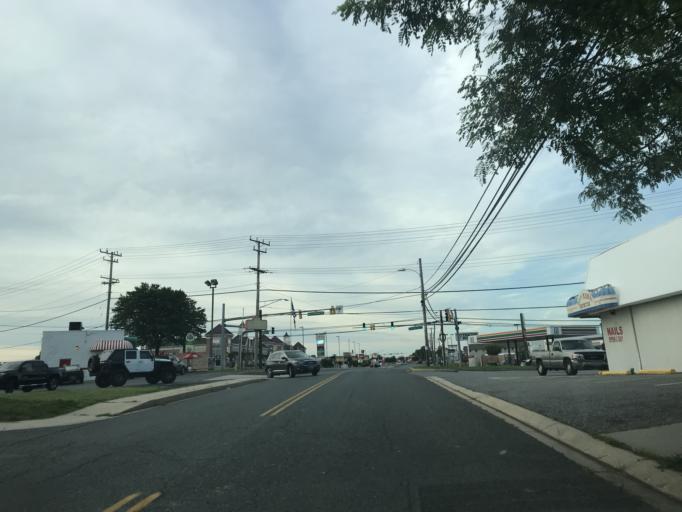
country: US
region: Maryland
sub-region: Harford County
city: Aberdeen
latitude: 39.5189
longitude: -76.1860
